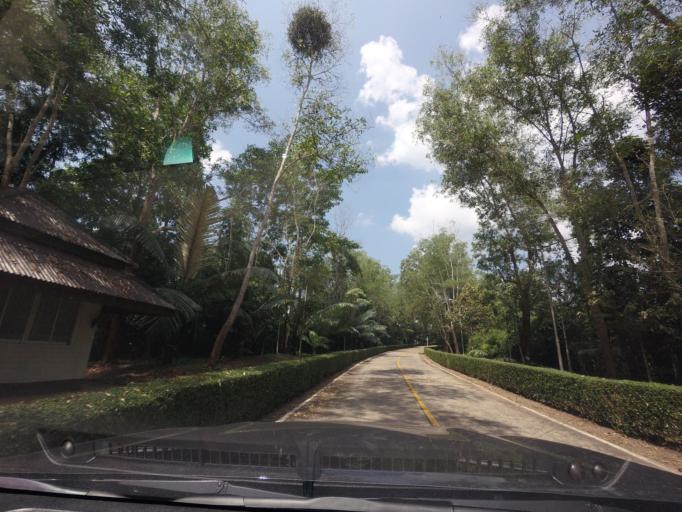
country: TH
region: Nan
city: Bo Kluea
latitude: 19.0203
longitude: 101.2084
